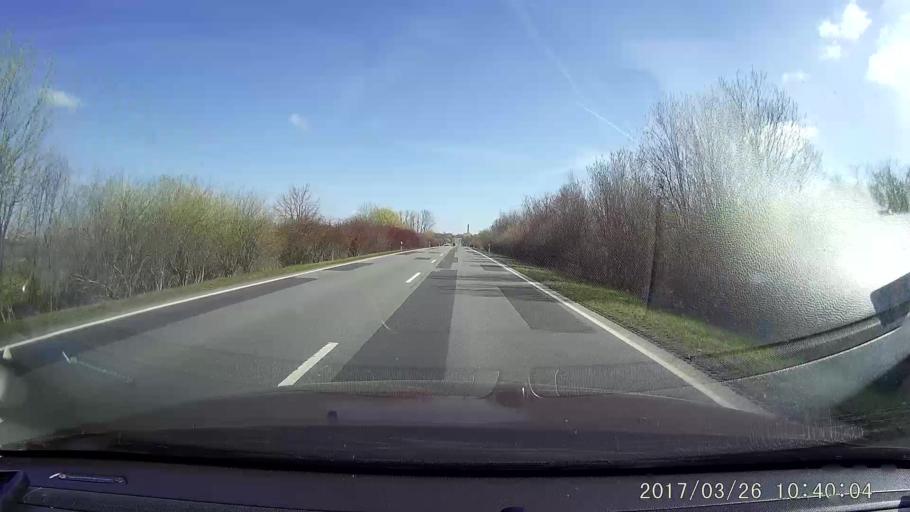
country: DE
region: Saxony
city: Goerlitz
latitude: 51.1529
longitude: 14.9377
